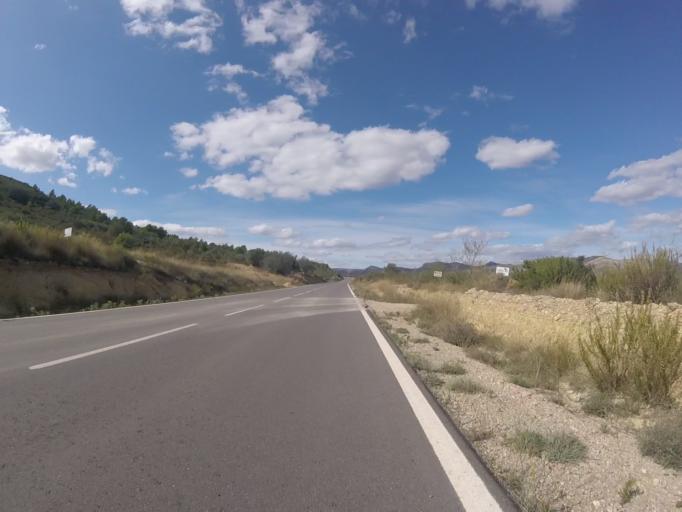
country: ES
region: Valencia
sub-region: Provincia de Castello
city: Chert/Xert
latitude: 40.4372
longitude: 0.1276
